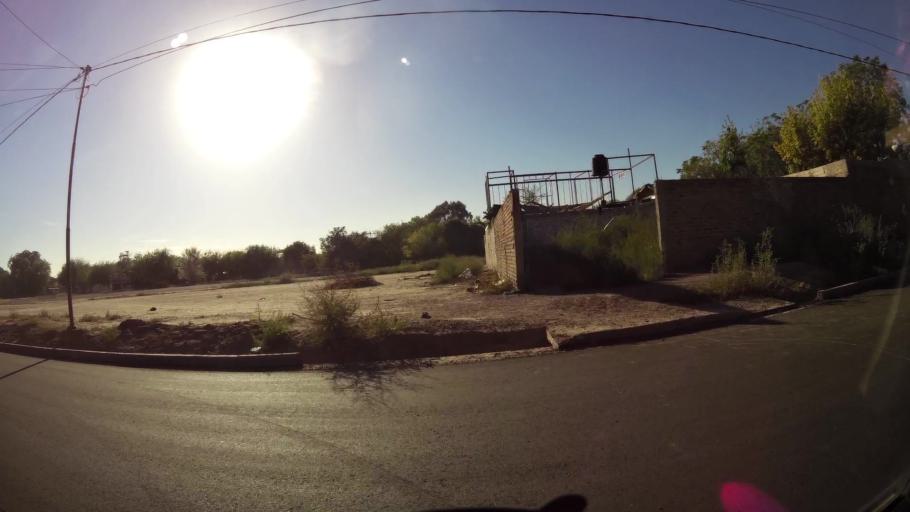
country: AR
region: Mendoza
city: Las Heras
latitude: -32.8572
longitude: -68.8180
